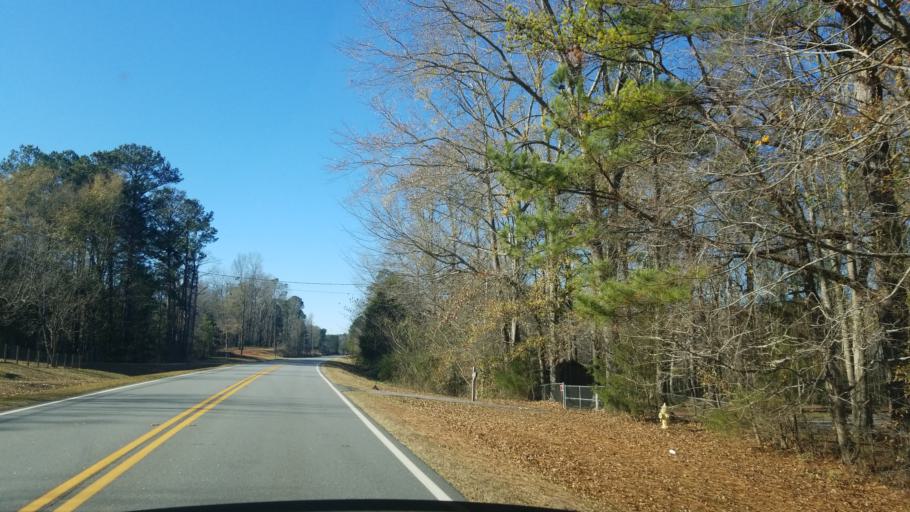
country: US
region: Georgia
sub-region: Harris County
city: Hamilton
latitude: 32.6681
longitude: -84.8959
